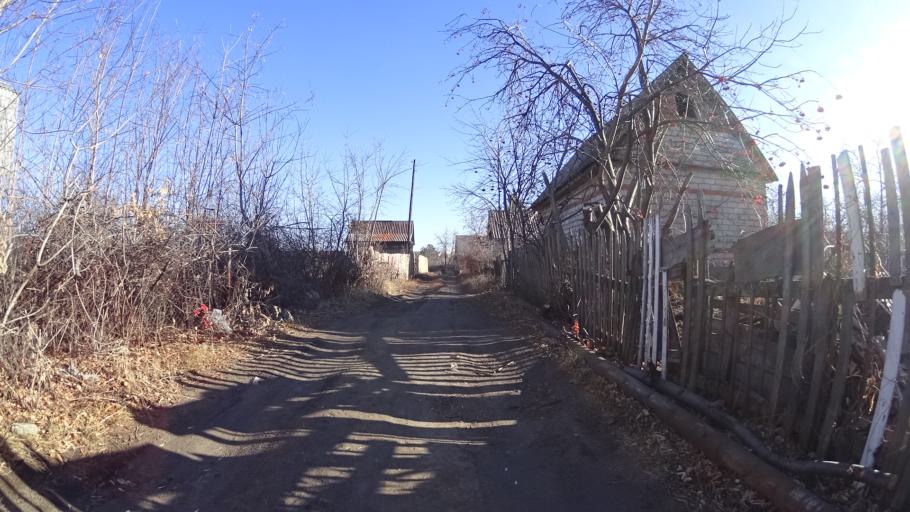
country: RU
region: Chelyabinsk
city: Troitsk
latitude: 54.0817
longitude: 61.5100
